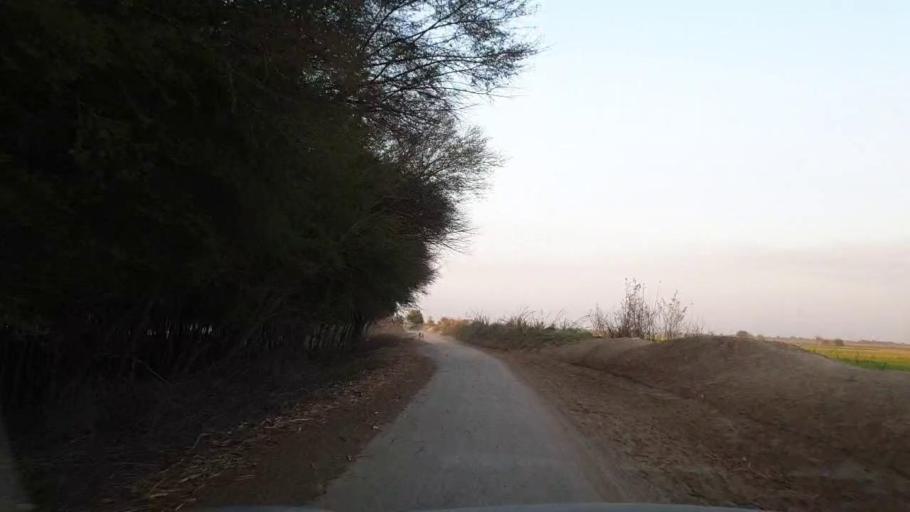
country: PK
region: Sindh
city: Berani
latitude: 25.6607
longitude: 68.7690
